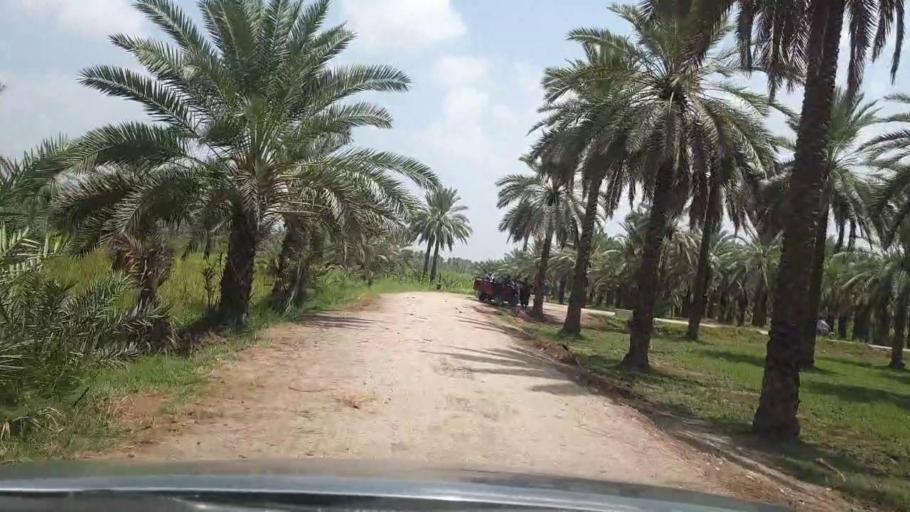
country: PK
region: Sindh
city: Khairpur
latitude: 27.6309
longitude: 68.7354
